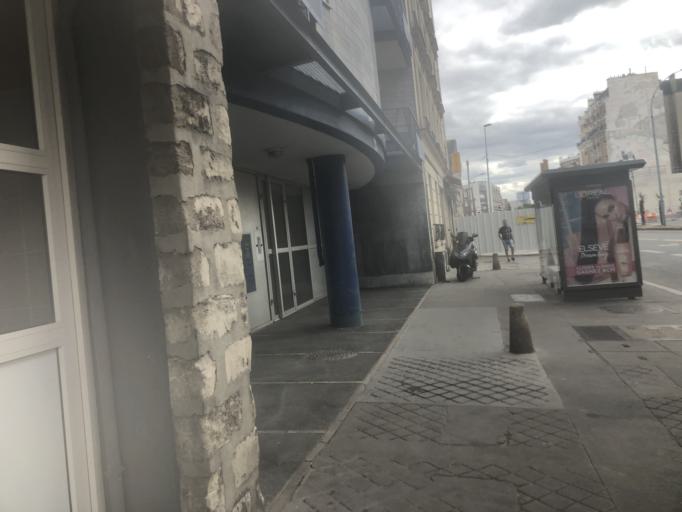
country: FR
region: Ile-de-France
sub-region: Paris
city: Saint-Ouen
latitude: 48.9133
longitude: 2.3356
